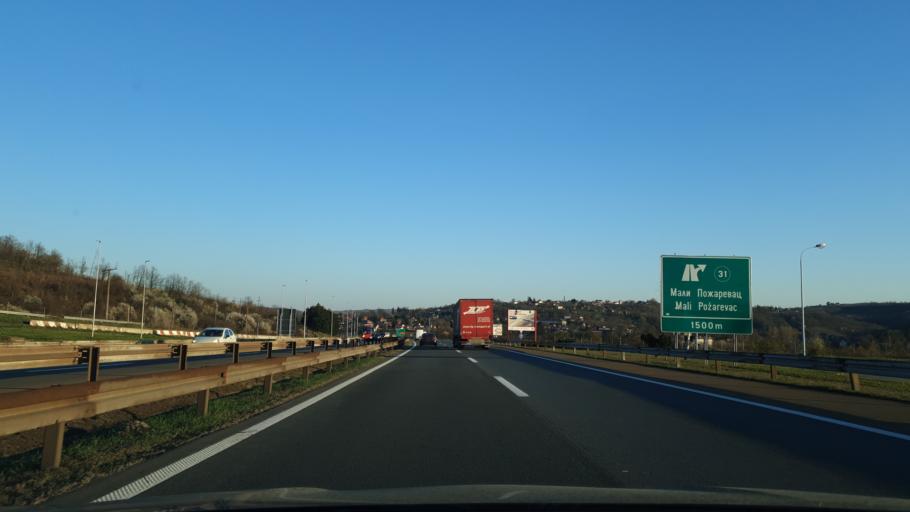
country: RS
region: Central Serbia
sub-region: Belgrade
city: Sopot
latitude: 44.5743
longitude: 20.6479
